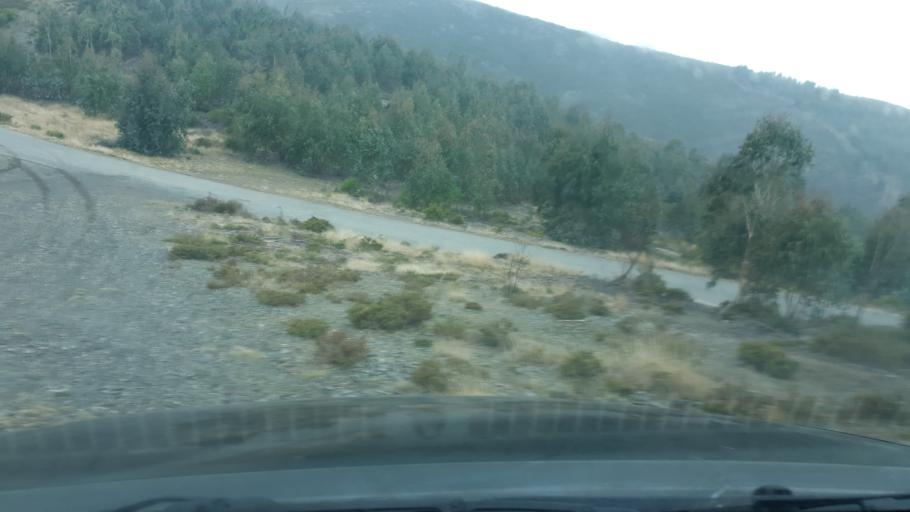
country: PT
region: Viseu
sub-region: Sao Pedro do Sul
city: Sao Pedro do Sul
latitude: 40.8573
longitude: -8.0987
